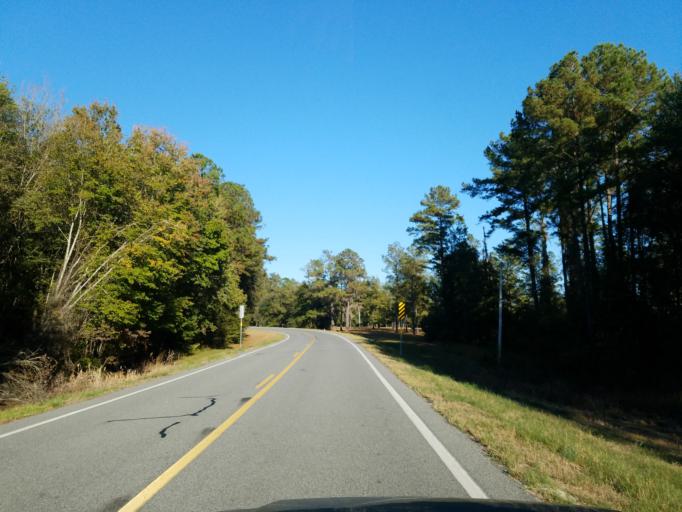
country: US
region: Georgia
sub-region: Echols County
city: Statenville
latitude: 30.6351
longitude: -83.0683
